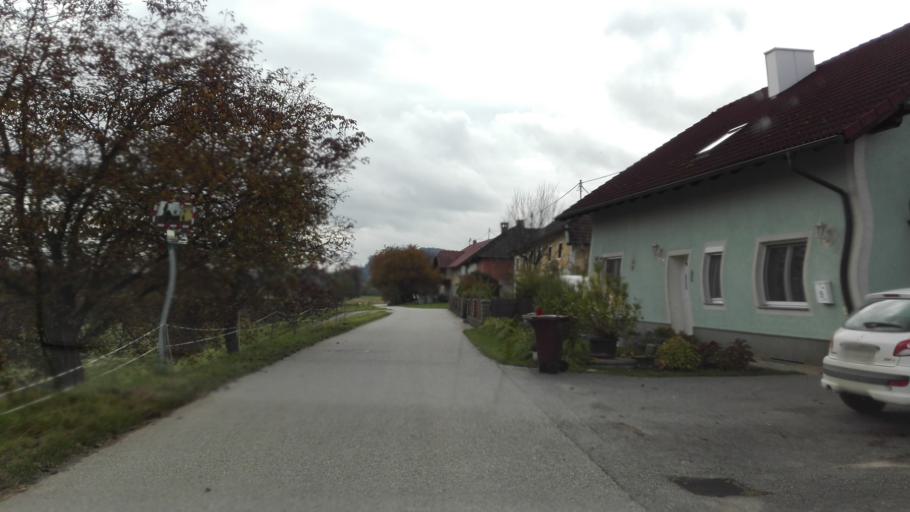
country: AT
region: Upper Austria
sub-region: Politischer Bezirk Urfahr-Umgebung
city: Feldkirchen an der Donau
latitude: 48.3482
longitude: 14.0081
